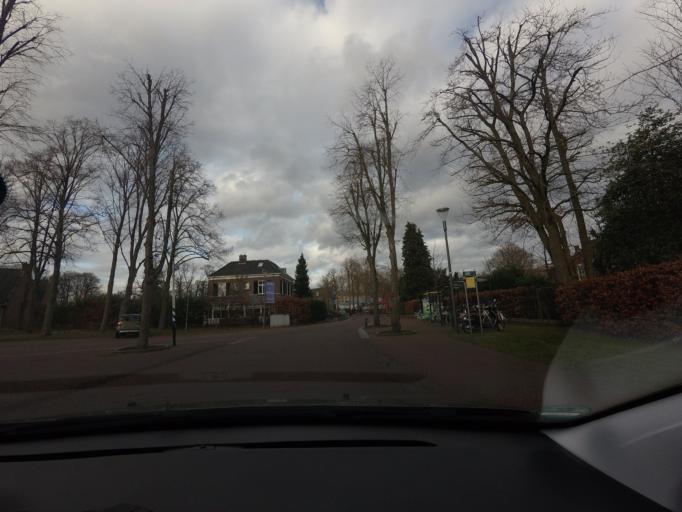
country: NL
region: Gelderland
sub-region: Gemeente Lochem
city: Gorssel
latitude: 52.1979
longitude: 6.1999
